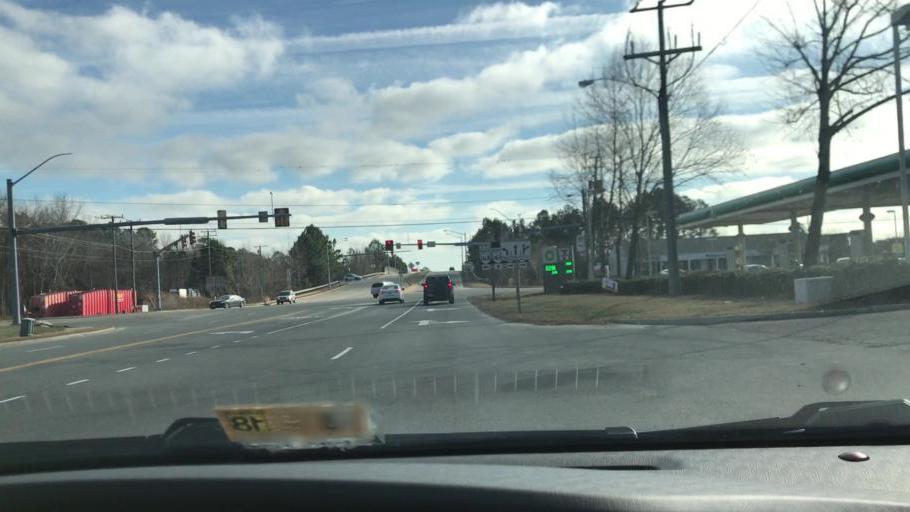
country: US
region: Virginia
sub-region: City of Chesapeake
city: Chesapeake
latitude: 36.6892
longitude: -76.2317
